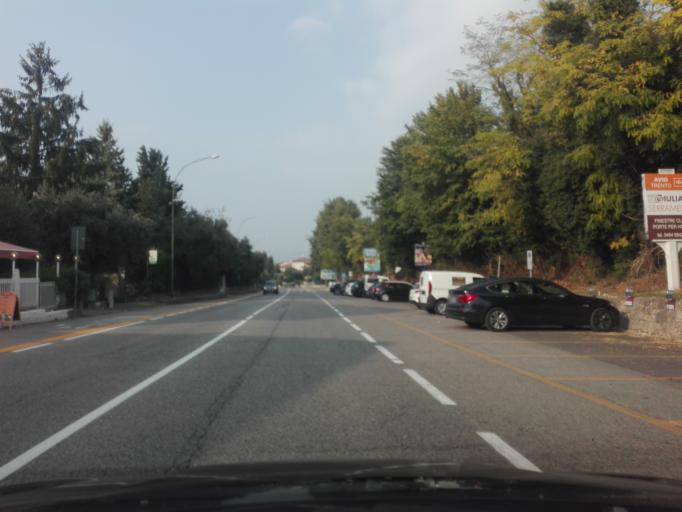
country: IT
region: Veneto
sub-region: Provincia di Verona
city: Lazise
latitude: 45.4996
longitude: 10.7373
